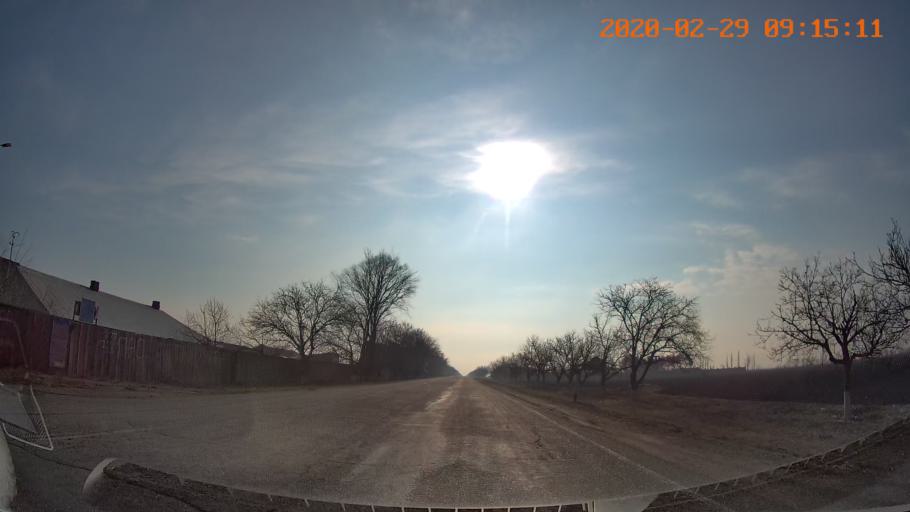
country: MD
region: Telenesti
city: Pervomaisc
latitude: 46.8027
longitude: 29.8647
